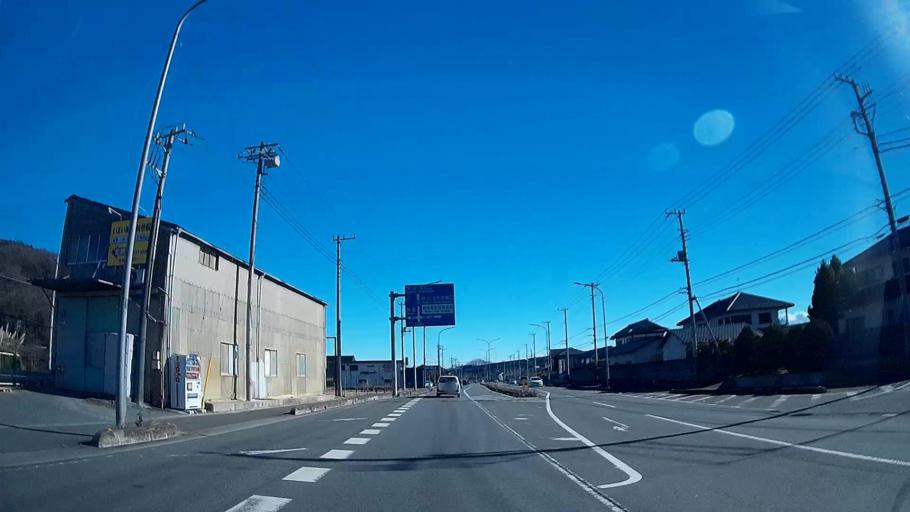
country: JP
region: Saitama
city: Yorii
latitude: 36.1192
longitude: 139.1680
